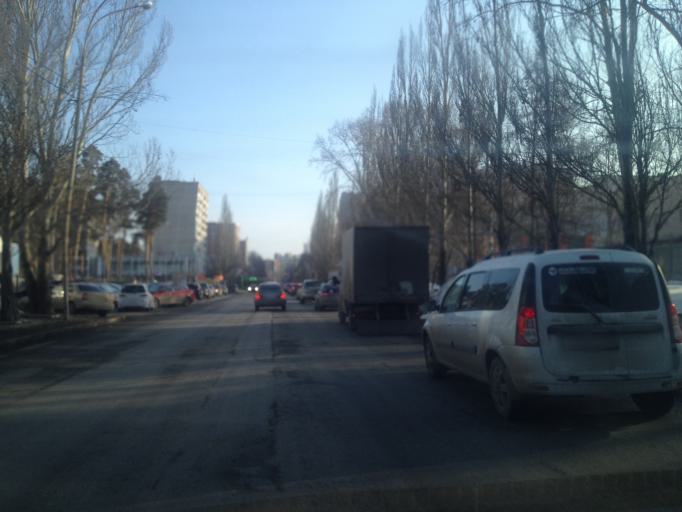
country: RU
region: Sverdlovsk
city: Sovkhoznyy
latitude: 56.8086
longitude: 60.5627
